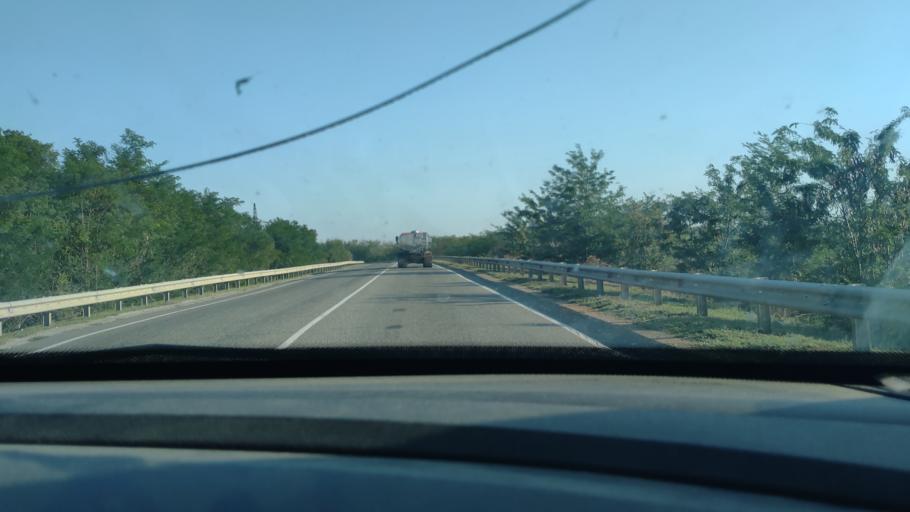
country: RU
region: Krasnodarskiy
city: Starominskaya
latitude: 46.5213
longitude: 39.0155
